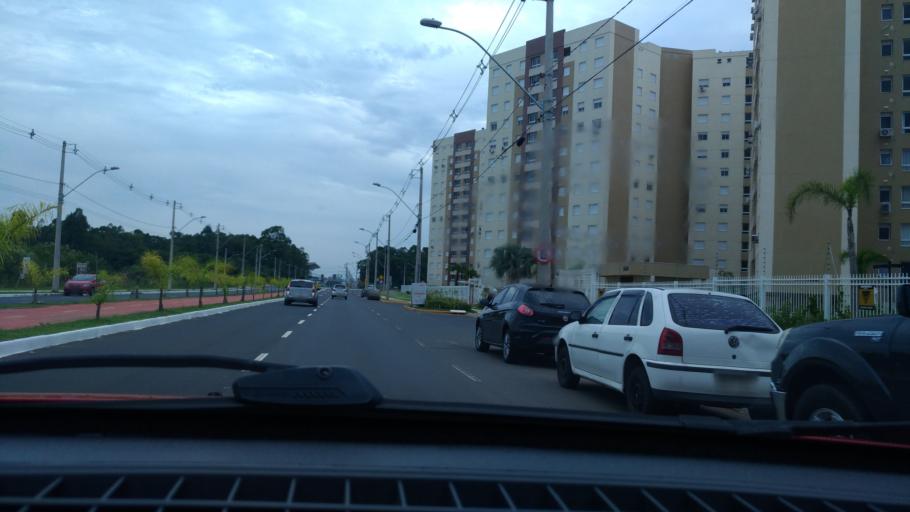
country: BR
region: Rio Grande do Sul
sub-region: Canoas
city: Canoas
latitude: -29.9081
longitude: -51.1652
